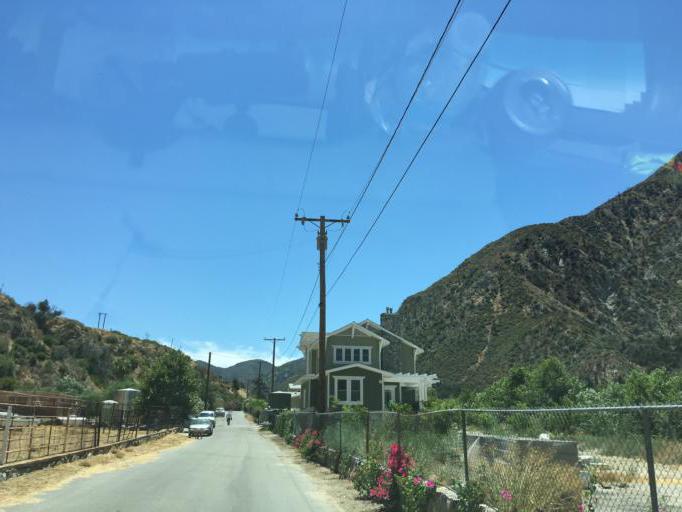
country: US
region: California
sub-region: Los Angeles County
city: La Crescenta-Montrose
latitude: 34.2911
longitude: -118.2341
